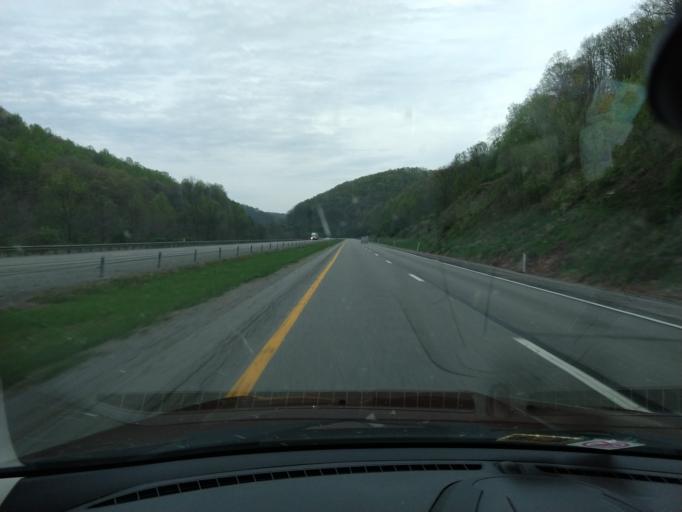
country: US
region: West Virginia
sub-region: Lewis County
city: Weston
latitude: 38.9837
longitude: -80.5075
